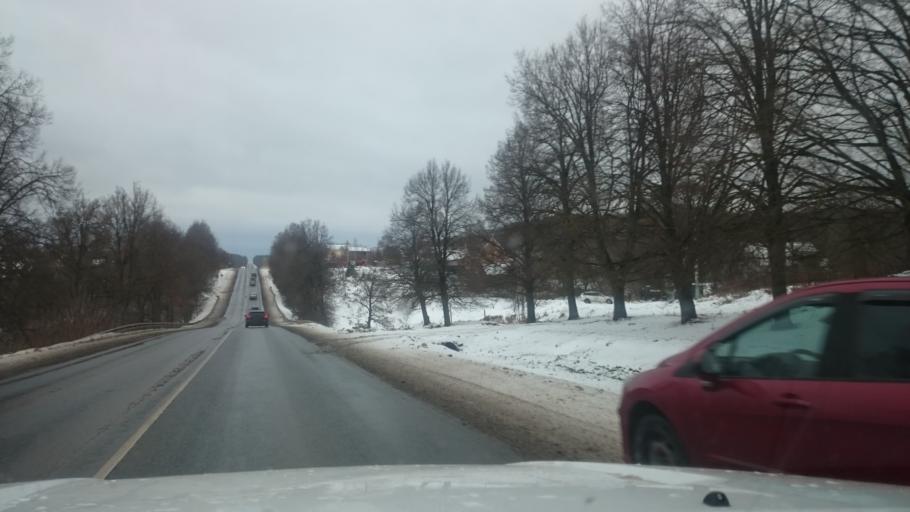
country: RU
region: Tula
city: Kosaya Gora
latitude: 54.1081
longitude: 37.5543
